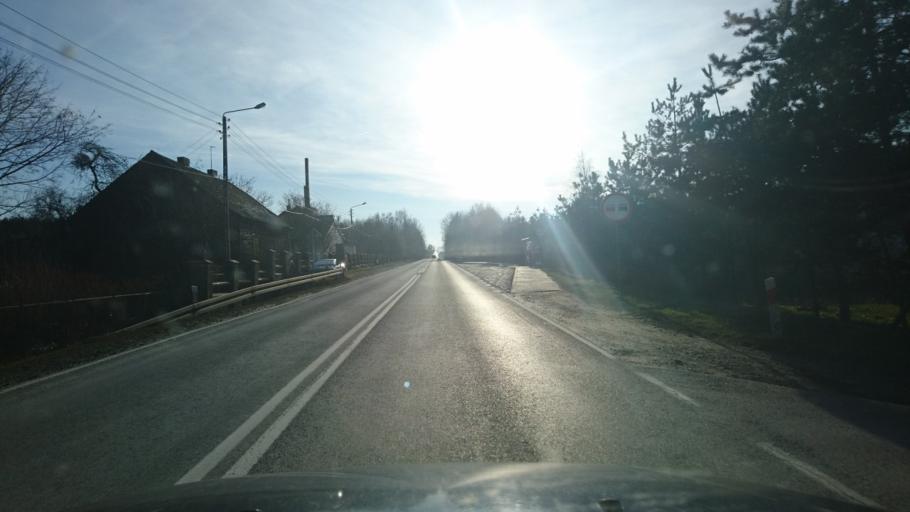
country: PL
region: Opole Voivodeship
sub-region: Powiat oleski
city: Dalachow
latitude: 51.0749
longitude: 18.6025
